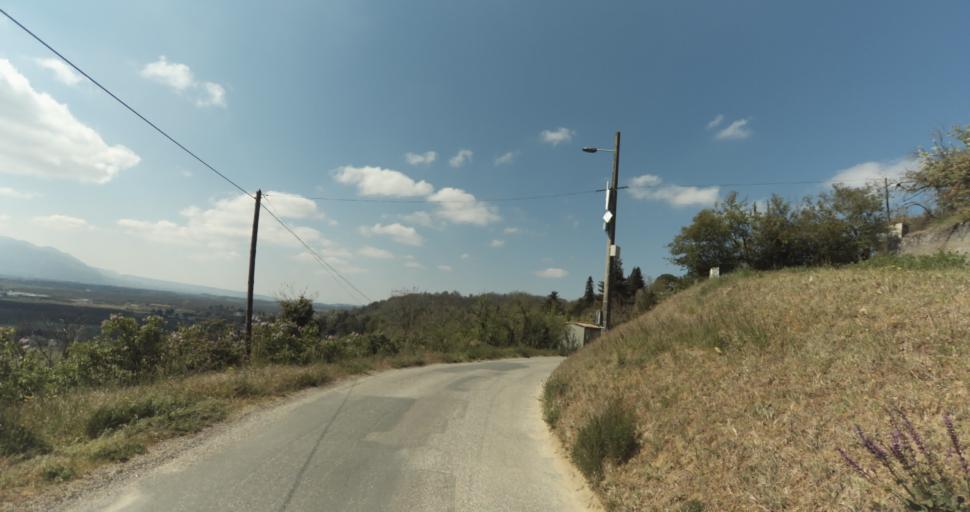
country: FR
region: Rhone-Alpes
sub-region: Departement de l'Isere
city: Saint-Marcellin
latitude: 45.1536
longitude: 5.3046
